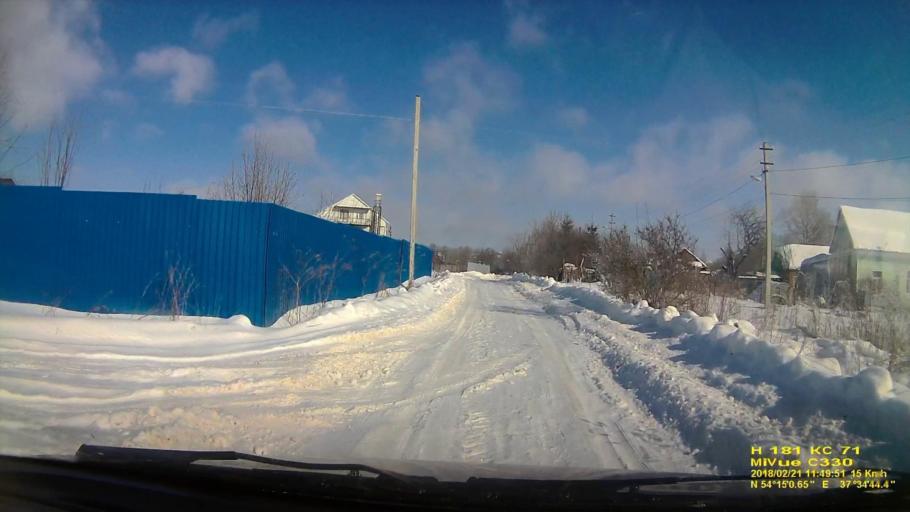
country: RU
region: Tula
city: Gorelki
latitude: 54.2505
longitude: 37.5796
